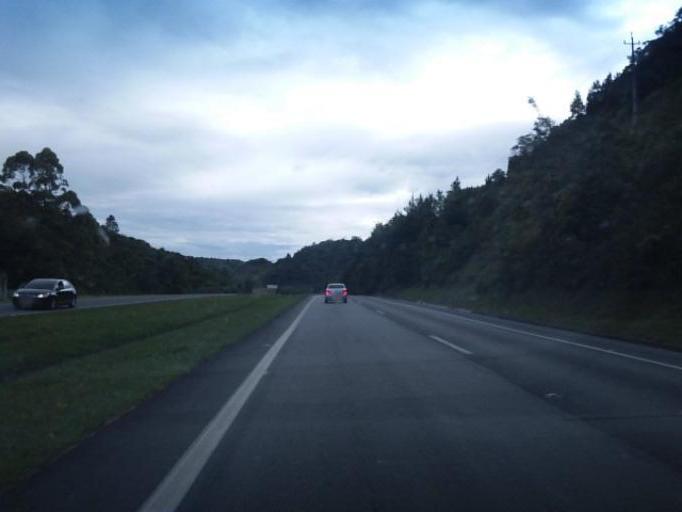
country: BR
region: Parana
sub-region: Campina Grande Do Sul
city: Campina Grande do Sul
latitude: -25.2536
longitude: -48.9116
